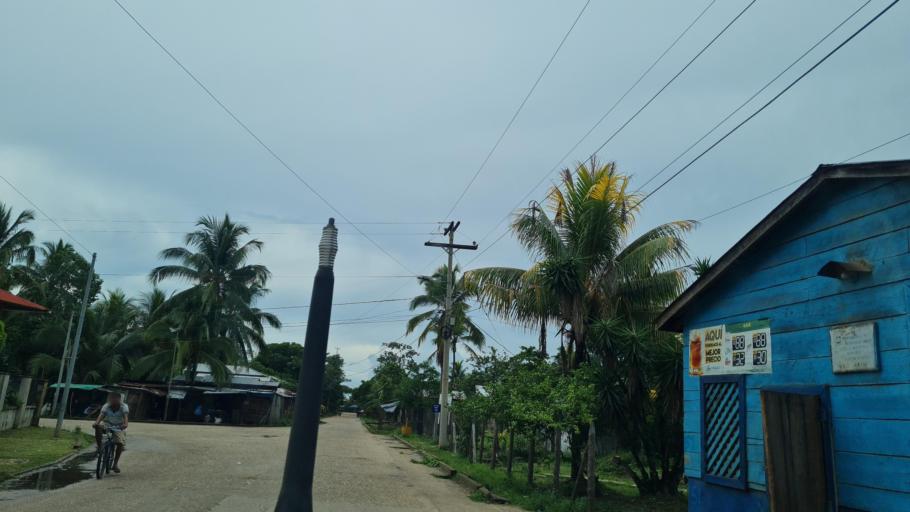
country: NI
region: Atlantico Norte (RAAN)
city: Waspam
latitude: 14.7355
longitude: -83.9695
